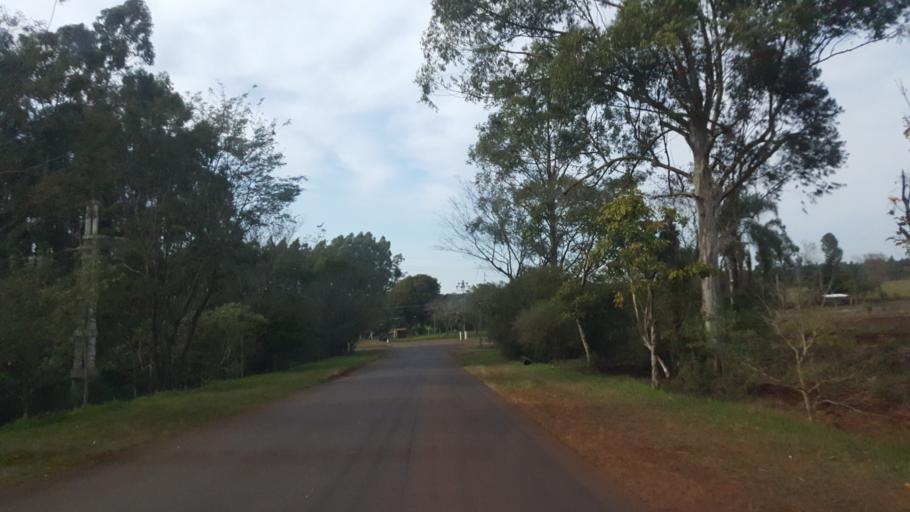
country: AR
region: Misiones
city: Capiovi
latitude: -26.9392
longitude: -55.0805
